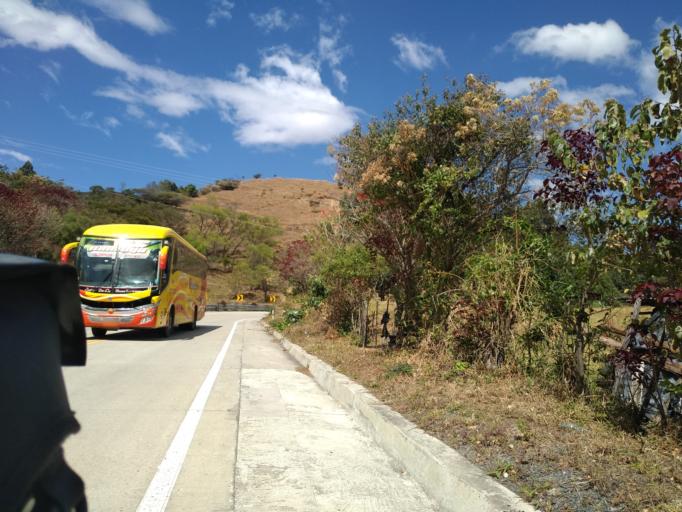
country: EC
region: Loja
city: Loja
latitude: -4.3462
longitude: -79.1893
